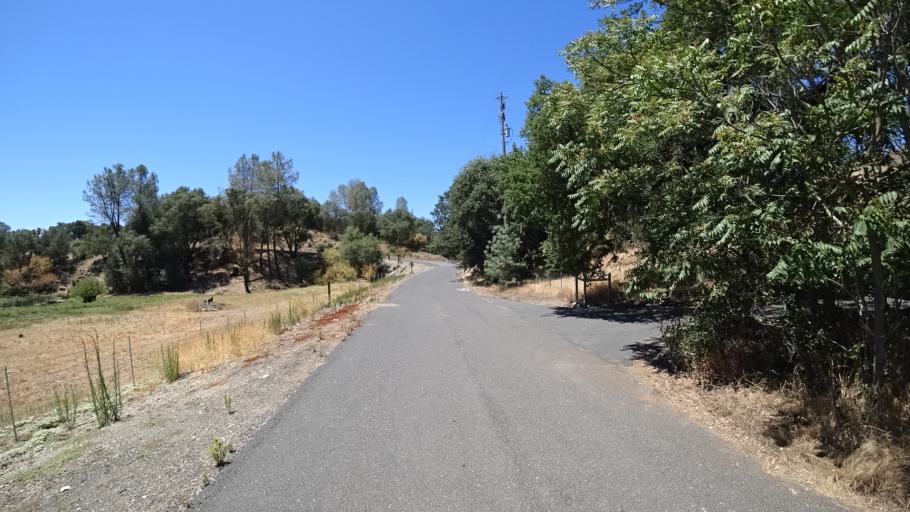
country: US
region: California
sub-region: Calaveras County
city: Copperopolis
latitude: 37.9641
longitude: -120.6848
